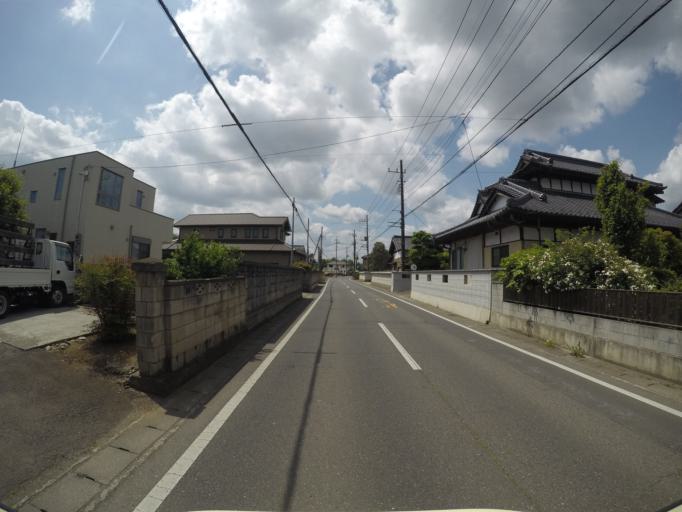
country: JP
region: Ibaraki
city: Naka
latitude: 36.0756
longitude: 140.0990
